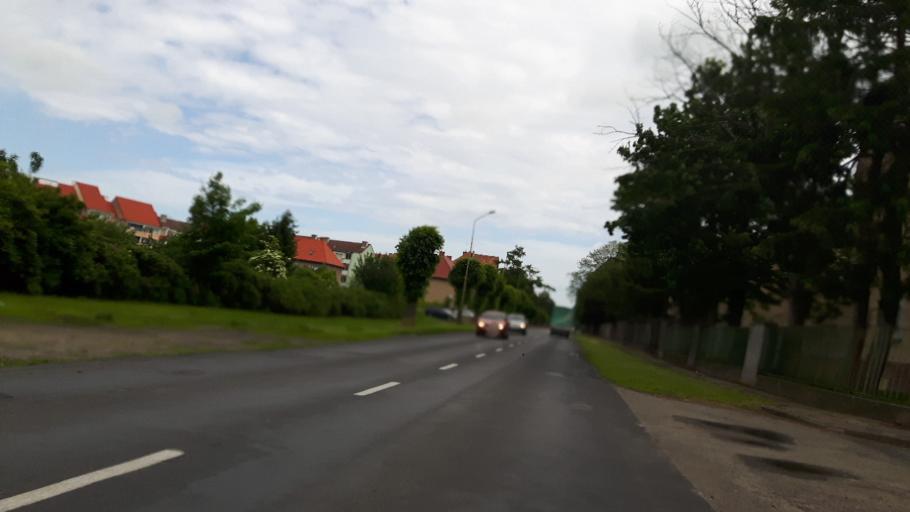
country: PL
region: West Pomeranian Voivodeship
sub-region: Powiat gryficki
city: Trzebiatow
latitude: 54.0520
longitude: 15.2564
